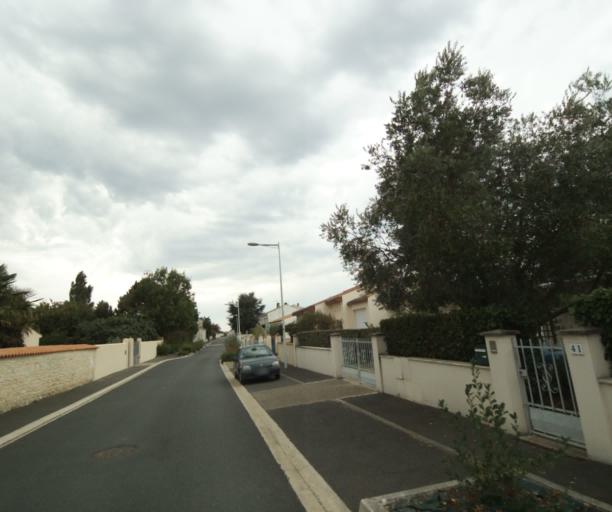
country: FR
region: Poitou-Charentes
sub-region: Departement de la Charente-Maritime
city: Tonnay-Charente
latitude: 45.9485
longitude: -0.8829
